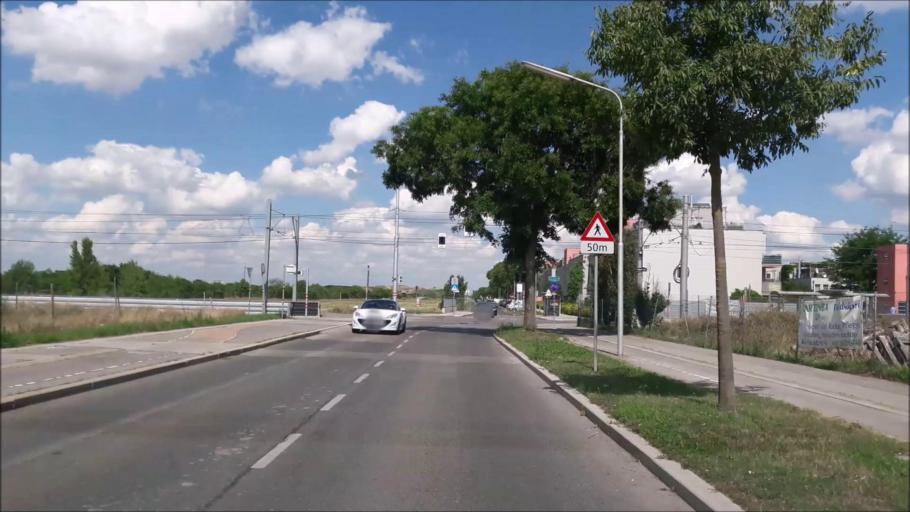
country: AT
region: Lower Austria
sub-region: Politischer Bezirk Wien-Umgebung
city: Gerasdorf bei Wien
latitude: 48.2427
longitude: 16.4684
